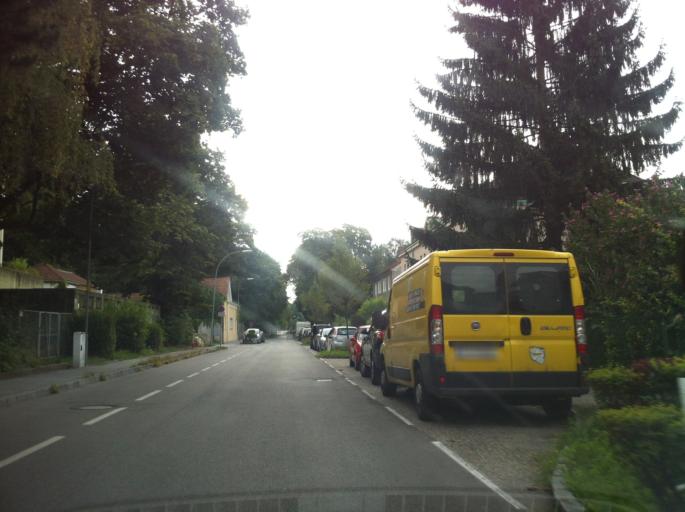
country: AT
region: Lower Austria
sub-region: Politischer Bezirk Wien-Umgebung
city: Purkersdorf
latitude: 48.2095
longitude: 16.1812
